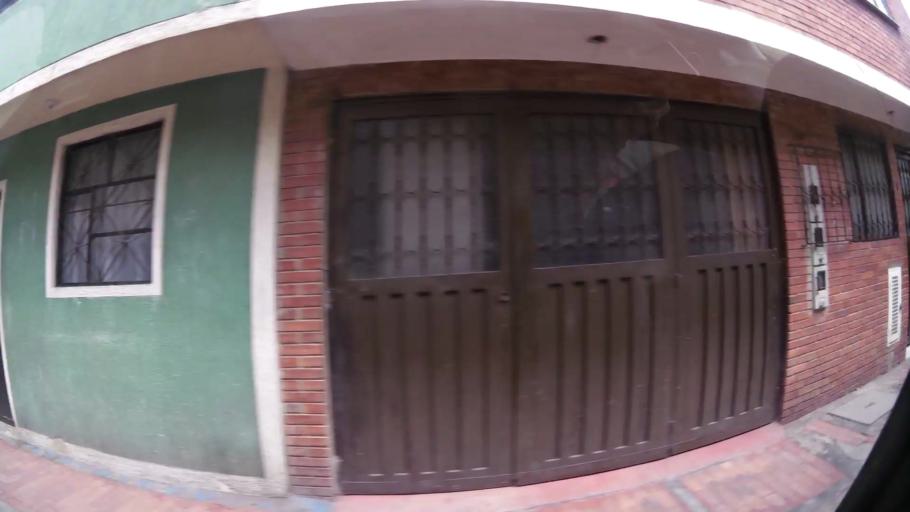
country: CO
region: Cundinamarca
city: Cota
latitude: 4.7276
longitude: -74.0924
